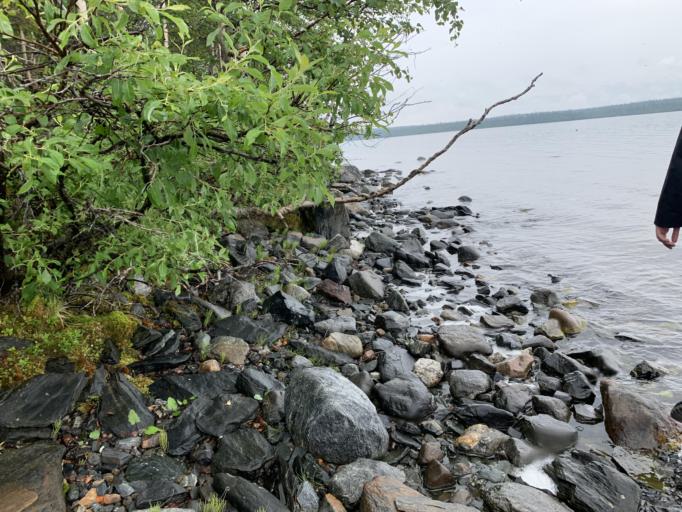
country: RU
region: Murmansk
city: Monchegorsk
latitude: 67.6901
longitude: 32.9716
